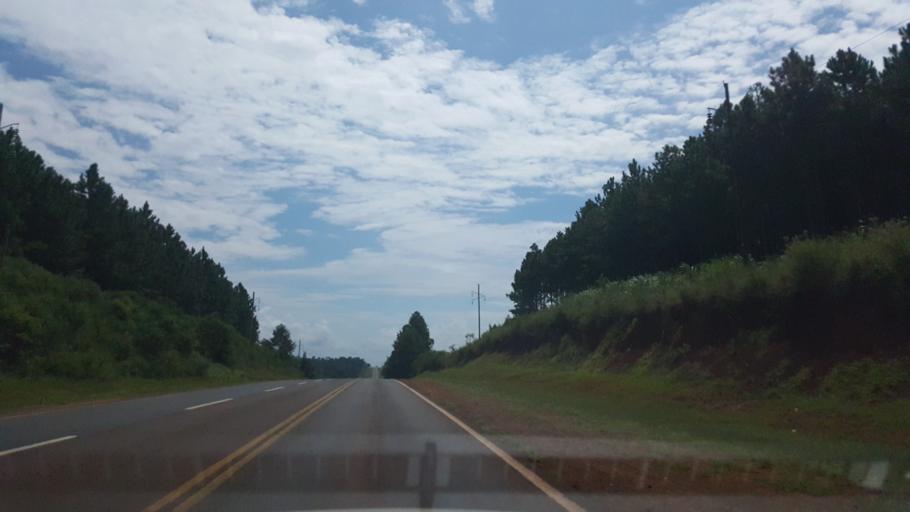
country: AR
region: Misiones
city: Capiovi
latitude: -26.9017
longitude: -55.0603
